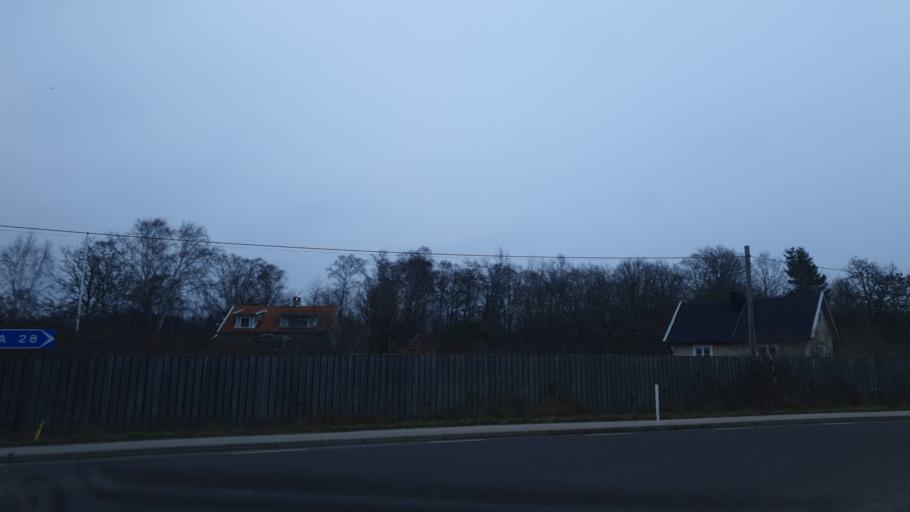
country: SE
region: Blekinge
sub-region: Karlskrona Kommun
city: Sturko
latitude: 56.1152
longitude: 15.6555
